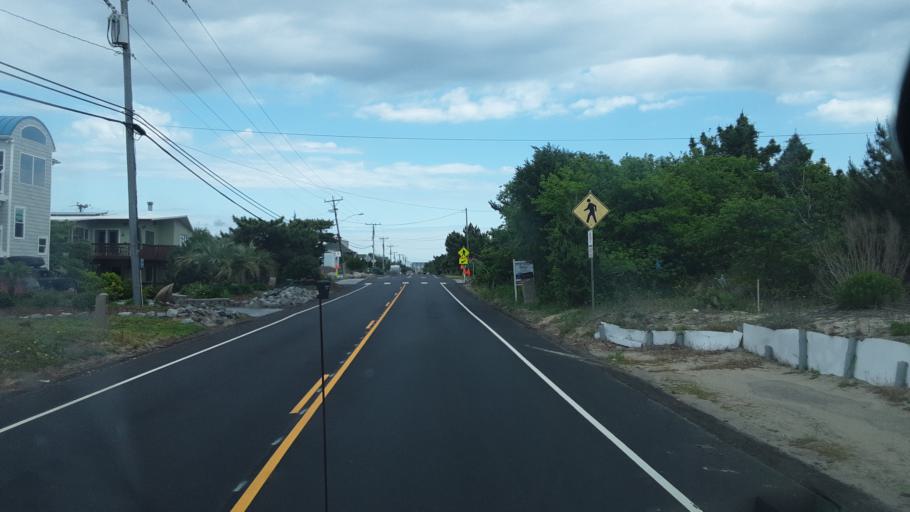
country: US
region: Virginia
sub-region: City of Virginia Beach
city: Virginia Beach
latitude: 36.7325
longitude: -75.9401
